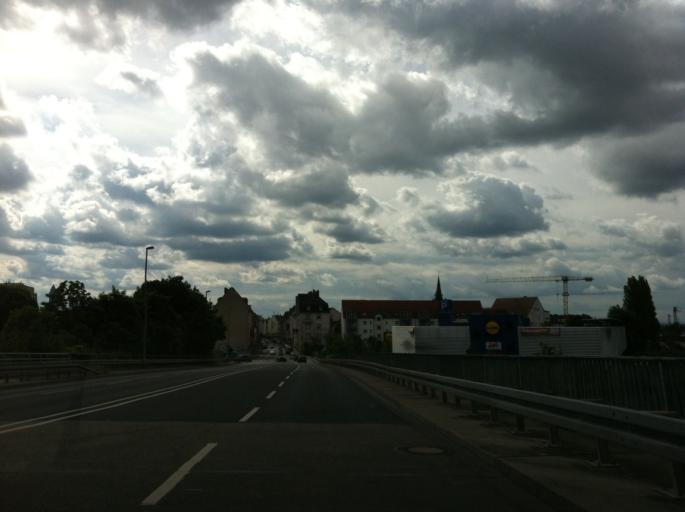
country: DE
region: Hesse
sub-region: Regierungsbezirk Darmstadt
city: Eschborn
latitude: 50.1290
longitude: 8.6059
